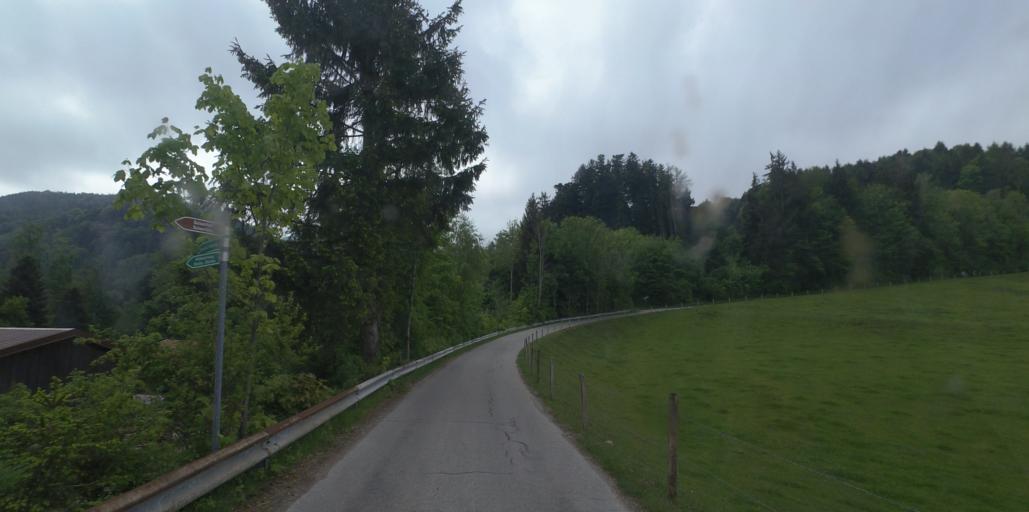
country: DE
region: Bavaria
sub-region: Upper Bavaria
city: Bernau am Chiemsee
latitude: 47.7955
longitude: 12.3609
